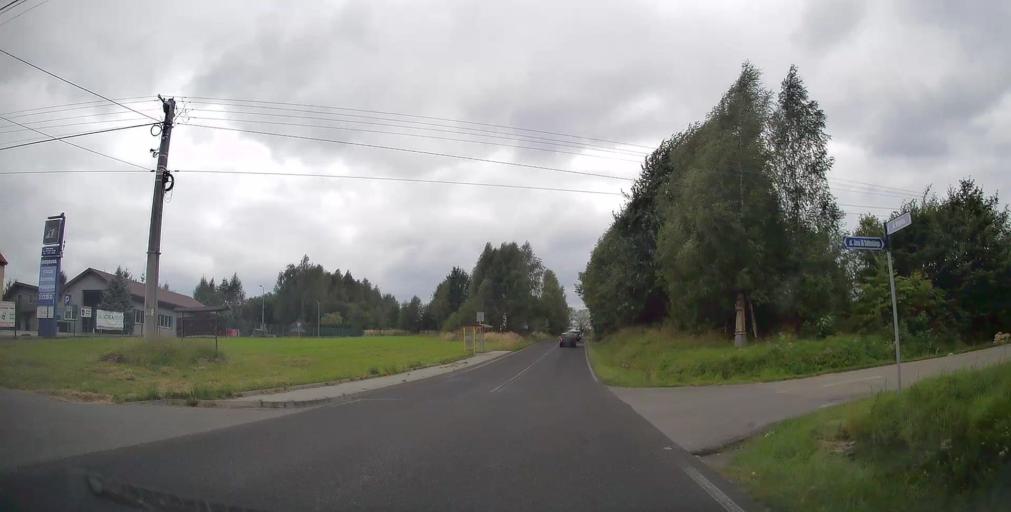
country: PL
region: Lesser Poland Voivodeship
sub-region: Powiat chrzanowski
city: Grojec
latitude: 50.0799
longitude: 19.5570
